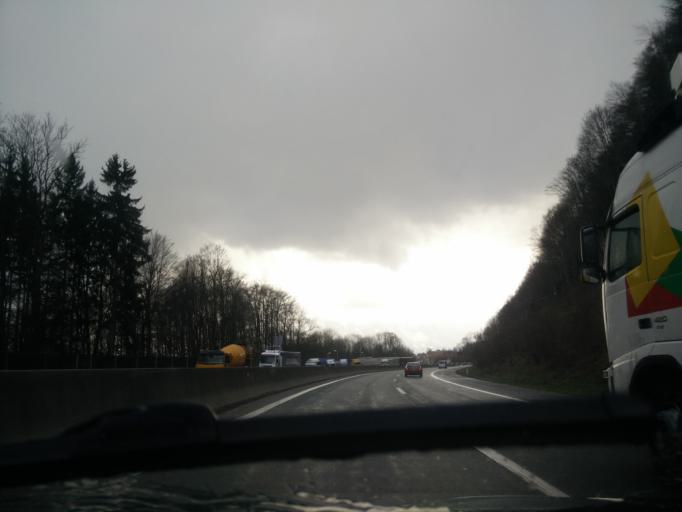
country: AT
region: Salzburg
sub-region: Politischer Bezirk Salzburg-Umgebung
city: Hallwang
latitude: 47.8413
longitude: 13.0783
